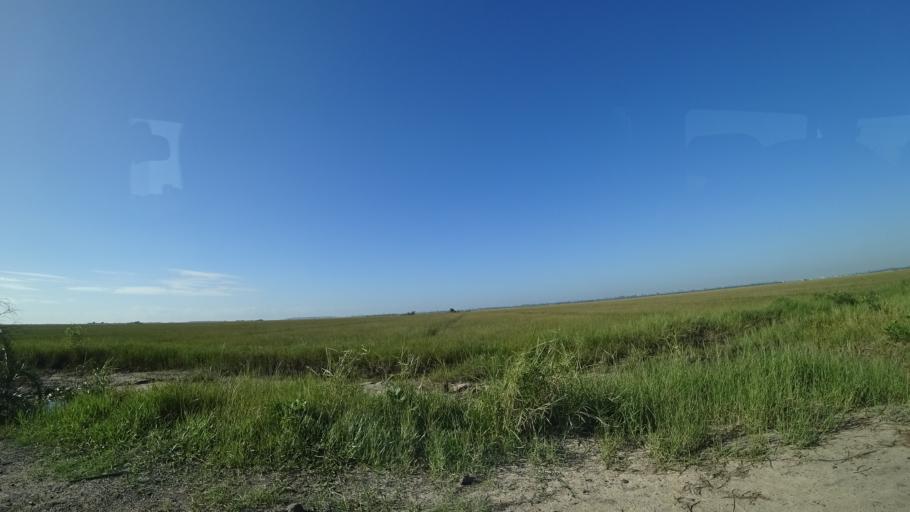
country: MZ
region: Sofala
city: Beira
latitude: -19.7570
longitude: 34.9215
